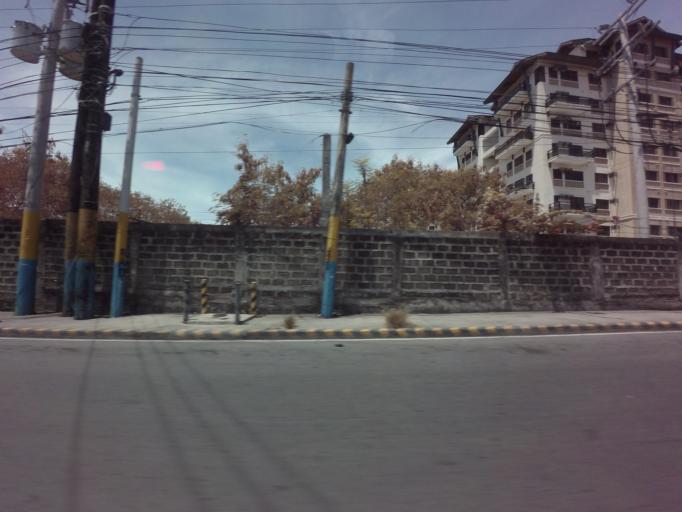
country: PH
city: Sambayanihan People's Village
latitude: 14.4527
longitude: 121.0494
